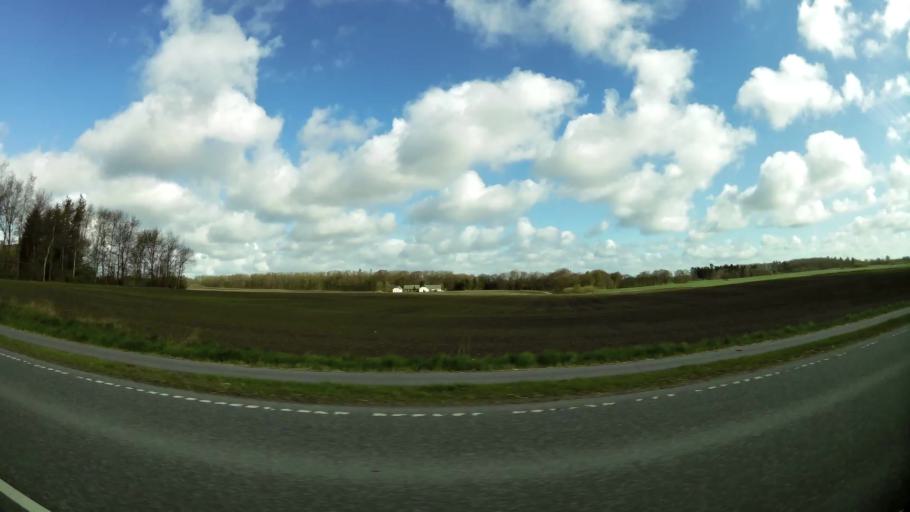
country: DK
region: North Denmark
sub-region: Mariagerfjord Kommune
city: Hobro
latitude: 56.6256
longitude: 9.8492
